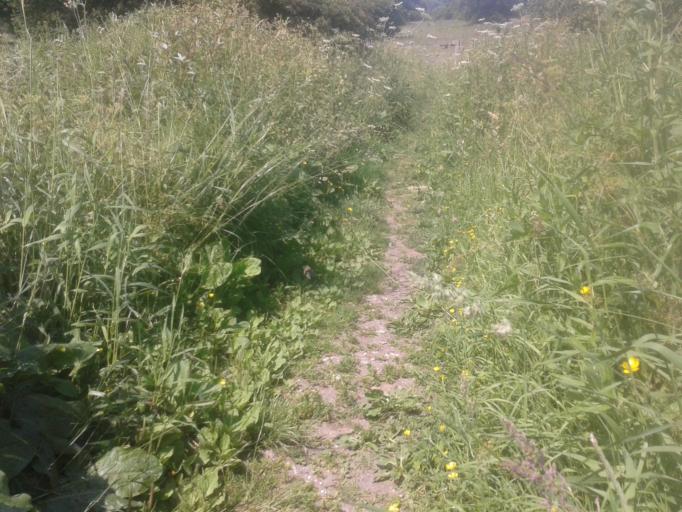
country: GB
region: England
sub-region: East Riding of Yorkshire
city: Londesborough
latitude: 53.8941
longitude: -0.6715
